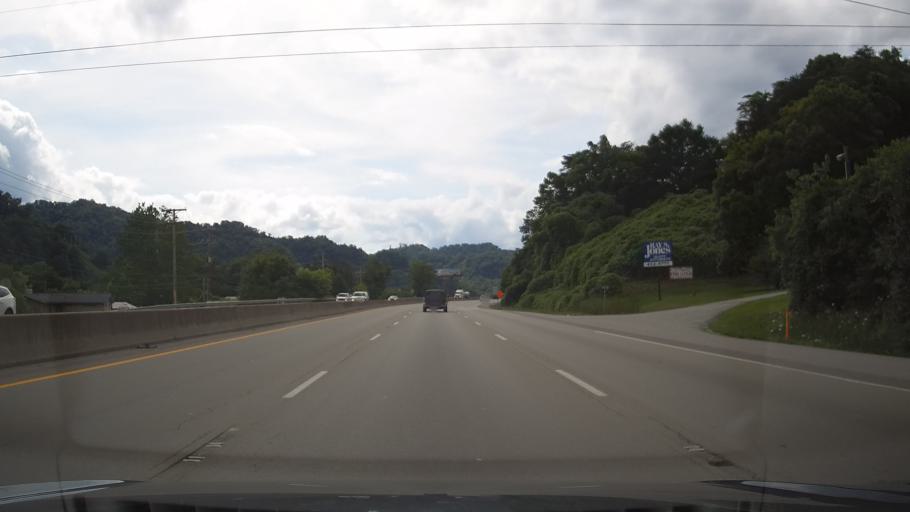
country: US
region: Kentucky
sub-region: Pike County
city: Coal Run Village
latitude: 37.5118
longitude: -82.5516
